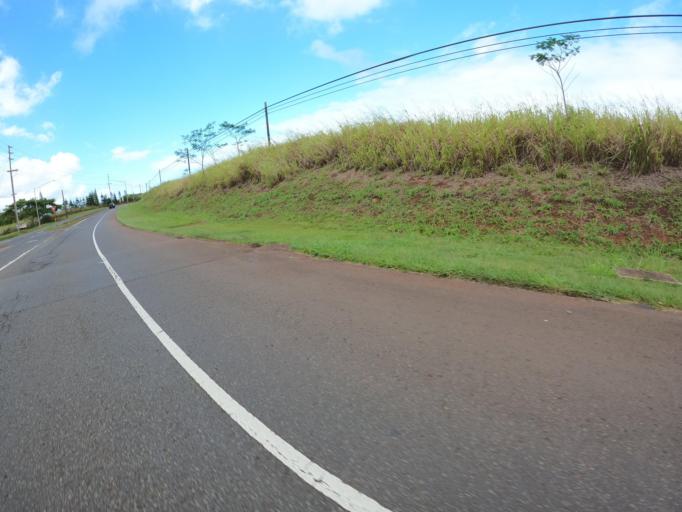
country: US
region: Hawaii
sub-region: Honolulu County
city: Whitmore Village
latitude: 21.5110
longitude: -158.0395
